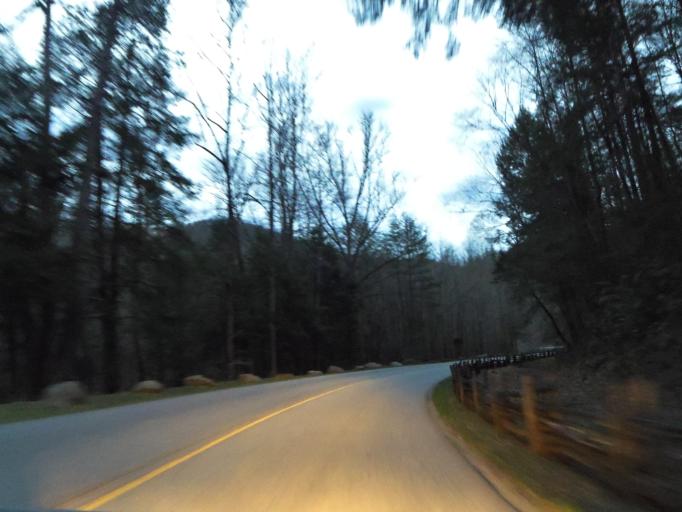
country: US
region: Tennessee
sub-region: Sevier County
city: Pigeon Forge
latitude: 35.6586
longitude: -83.7102
